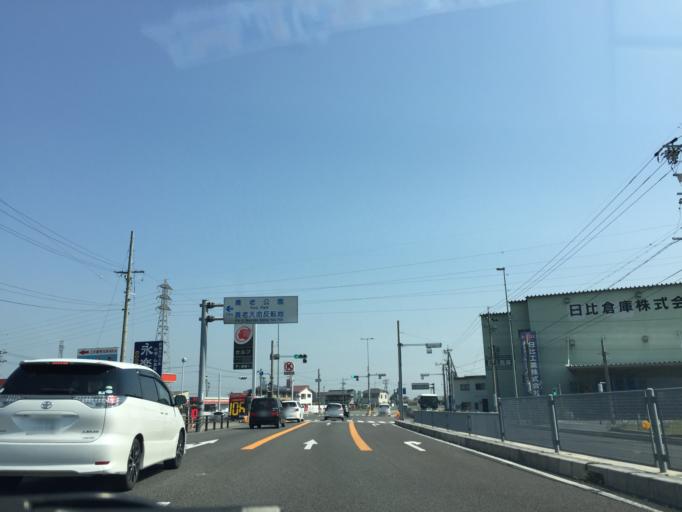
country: JP
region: Gifu
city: Ogaki
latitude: 35.2796
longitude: 136.5996
